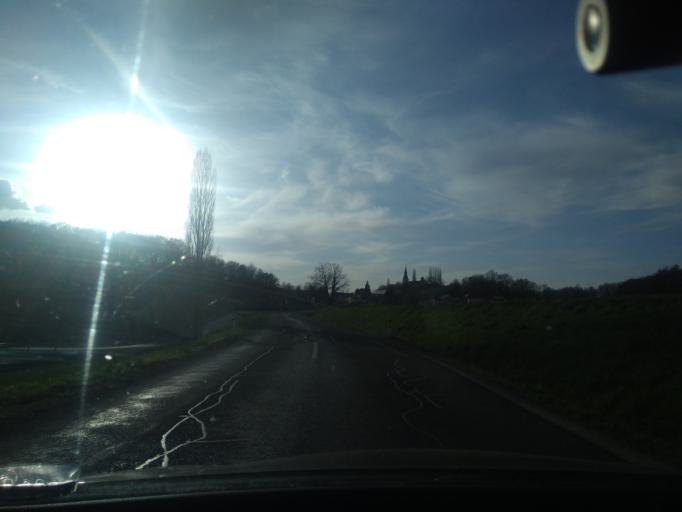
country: AT
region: Styria
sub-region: Politischer Bezirk Suedoststeiermark
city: Jagerberg
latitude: 46.8529
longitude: 15.7468
